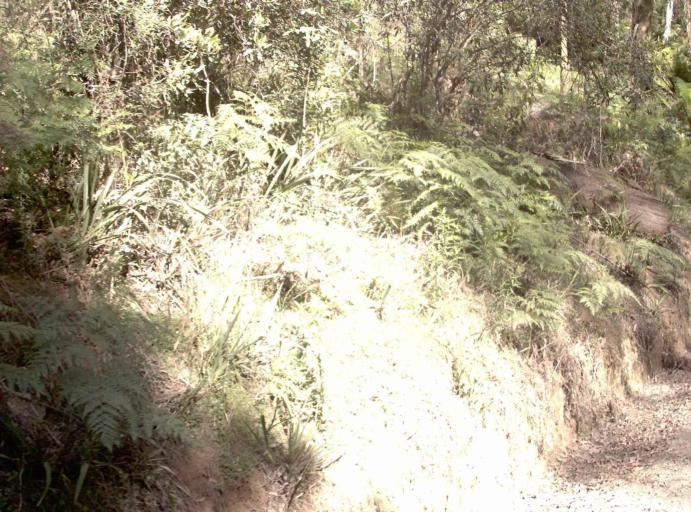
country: AU
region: New South Wales
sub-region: Bombala
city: Bombala
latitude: -37.2158
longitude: 148.7465
